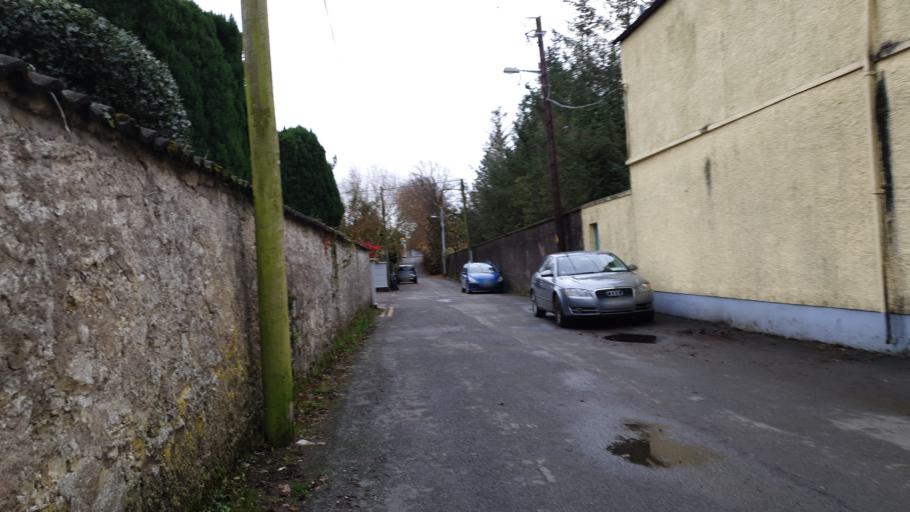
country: IE
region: Munster
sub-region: County Cork
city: Cork
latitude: 51.8980
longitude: -8.4286
